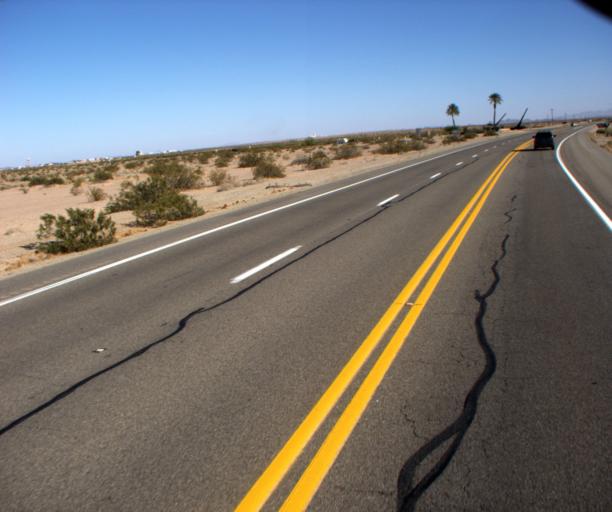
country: US
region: Arizona
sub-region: Yuma County
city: Fortuna Foothills
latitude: 32.8204
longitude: -114.3784
